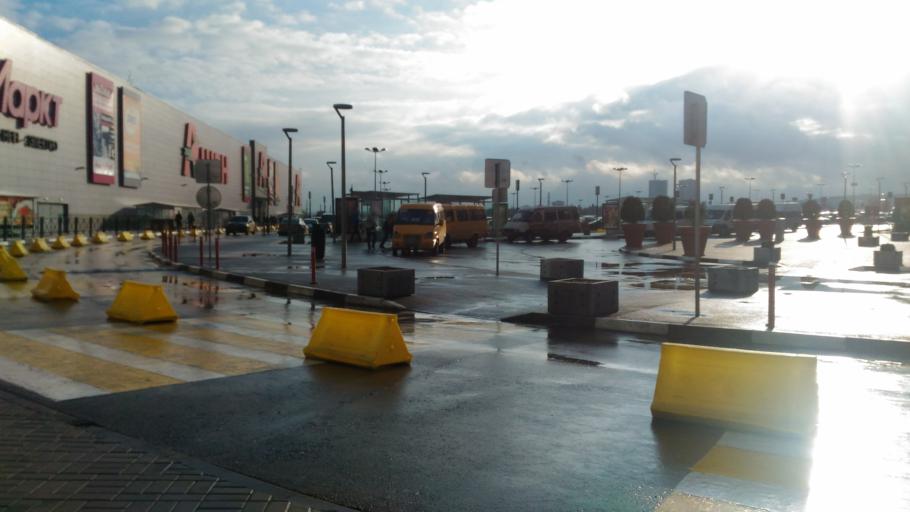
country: RU
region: Volgograd
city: Volgograd
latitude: 48.6372
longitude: 44.4349
